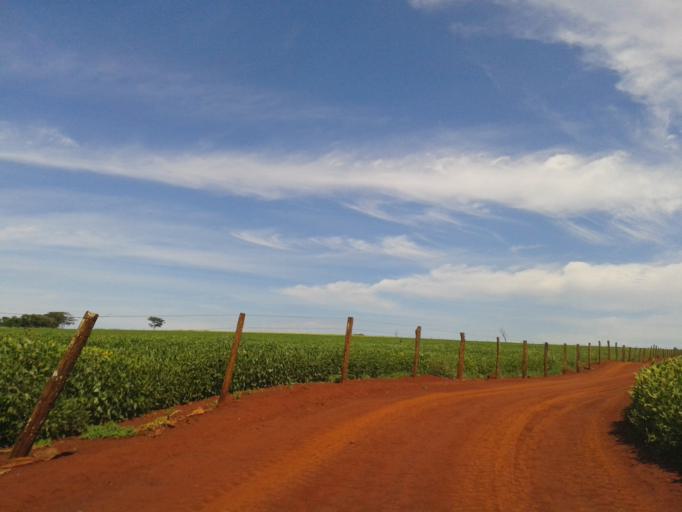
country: BR
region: Minas Gerais
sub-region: Capinopolis
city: Capinopolis
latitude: -18.6548
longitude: -49.7146
